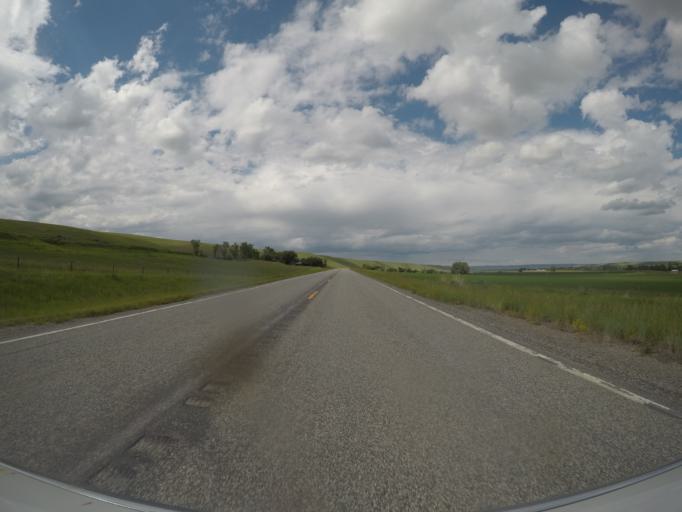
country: US
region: Montana
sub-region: Sweet Grass County
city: Big Timber
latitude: 45.7634
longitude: -109.9899
